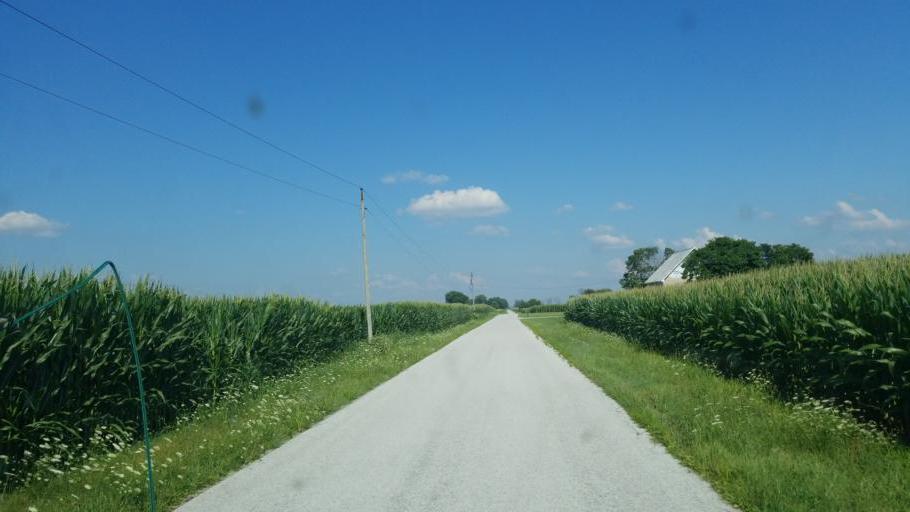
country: US
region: Ohio
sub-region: Hardin County
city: Kenton
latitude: 40.6875
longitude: -83.5290
